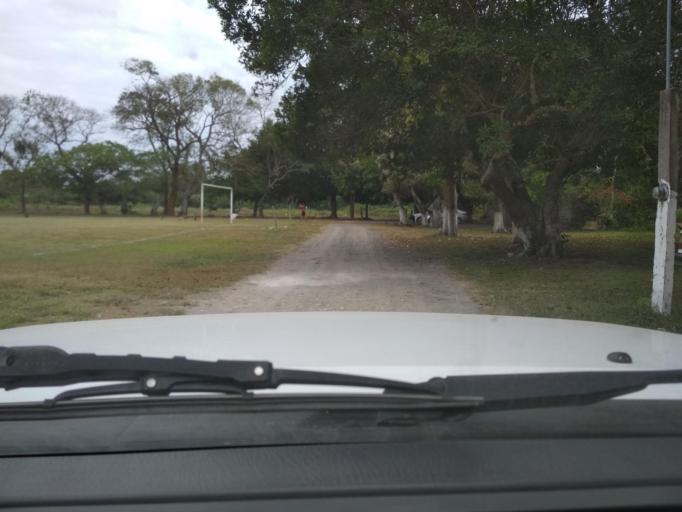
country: MX
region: Veracruz
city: El Tejar
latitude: 19.0698
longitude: -96.1428
